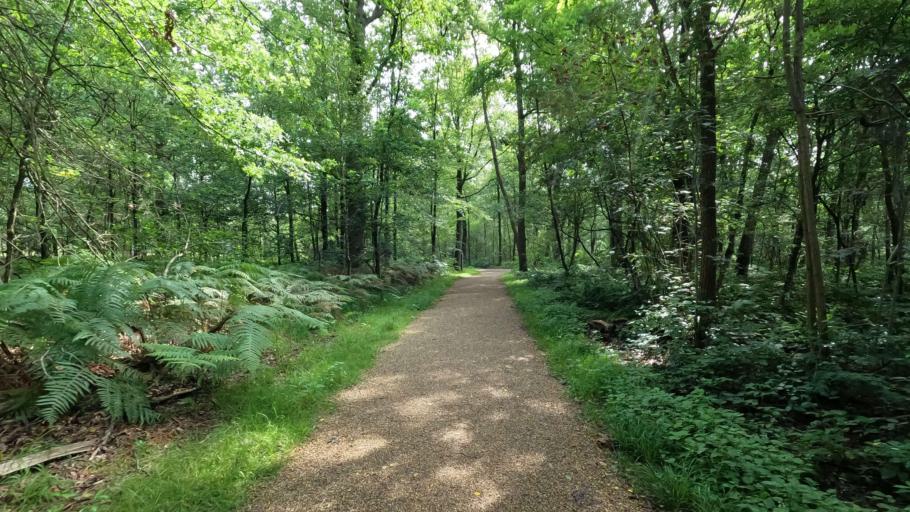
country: BE
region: Flanders
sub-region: Provincie Antwerpen
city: Heist-op-den-Berg
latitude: 51.0909
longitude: 4.7074
